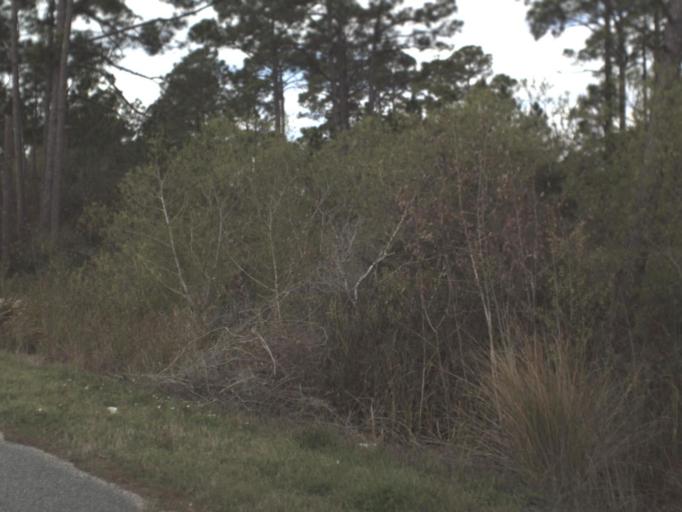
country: US
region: Florida
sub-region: Franklin County
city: Carrabelle
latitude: 29.7960
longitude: -84.7476
